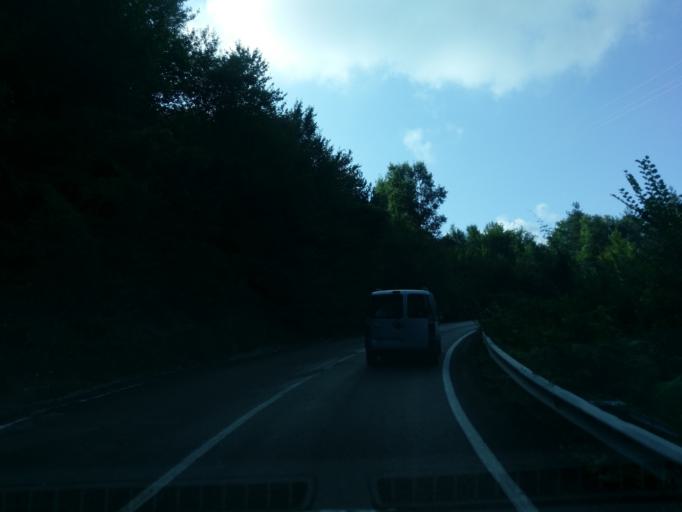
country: TR
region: Sinop
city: Ayancik
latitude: 41.8811
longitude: 34.5181
